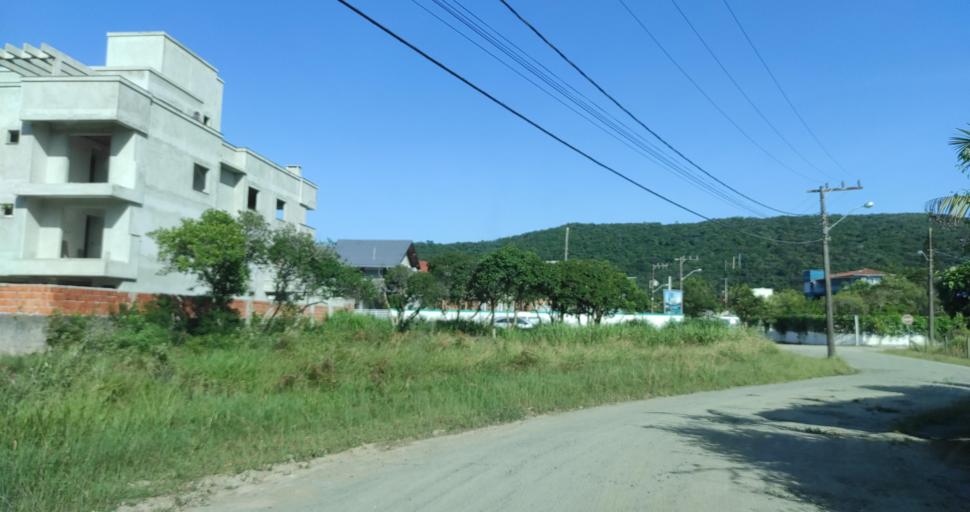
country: BR
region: Santa Catarina
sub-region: Porto Belo
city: Porto Belo
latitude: -27.1750
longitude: -48.5020
